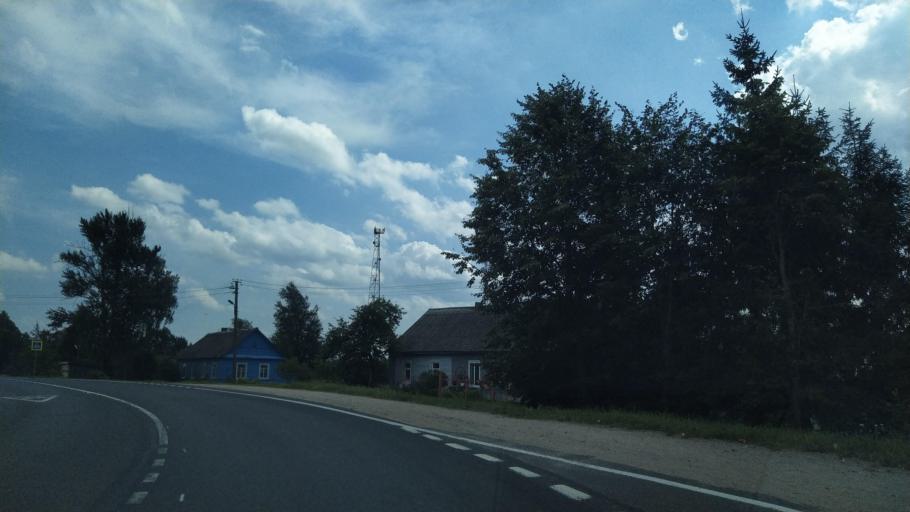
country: RU
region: Pskov
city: Pskov
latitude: 57.7560
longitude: 28.7714
